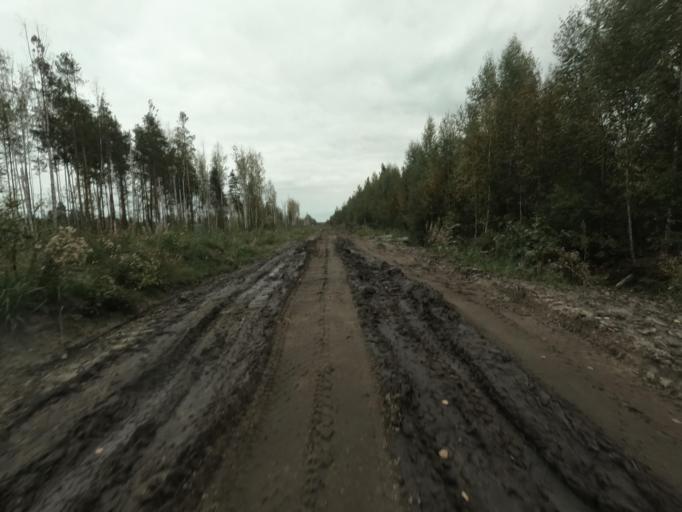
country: RU
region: St.-Petersburg
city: Sapernyy
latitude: 59.7562
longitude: 30.7074
